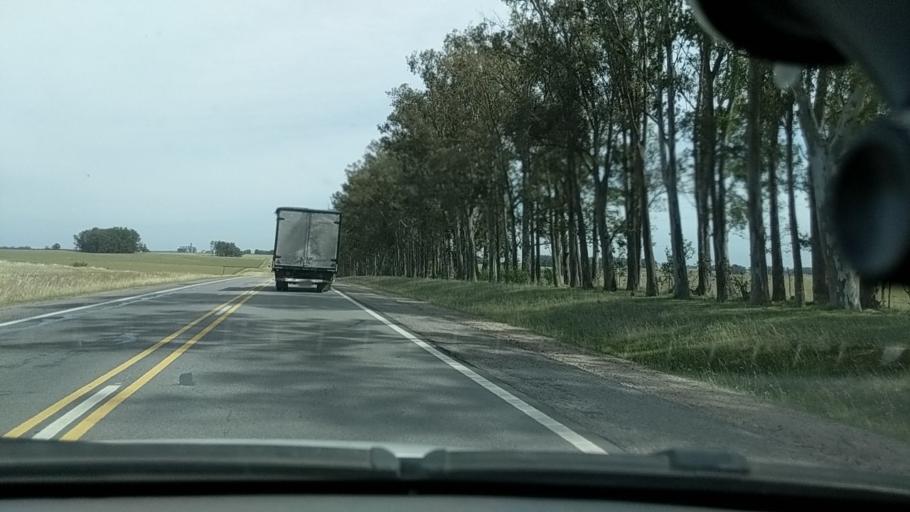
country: UY
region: Durazno
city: Durazno
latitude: -33.5158
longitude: -56.4105
